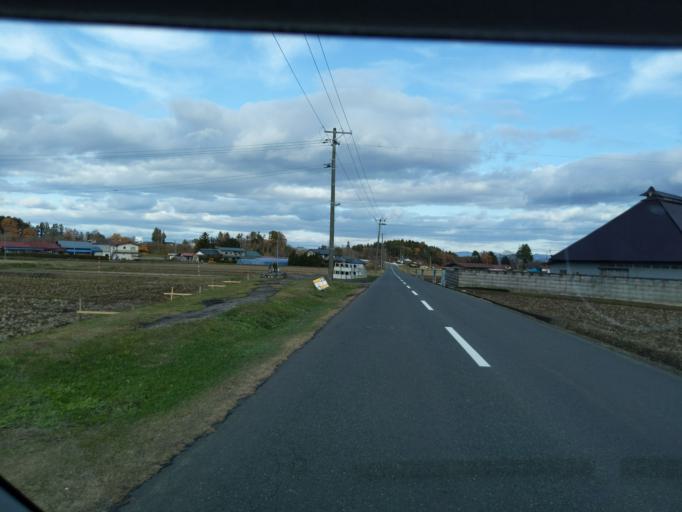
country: JP
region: Iwate
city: Mizusawa
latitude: 39.1804
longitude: 141.1018
